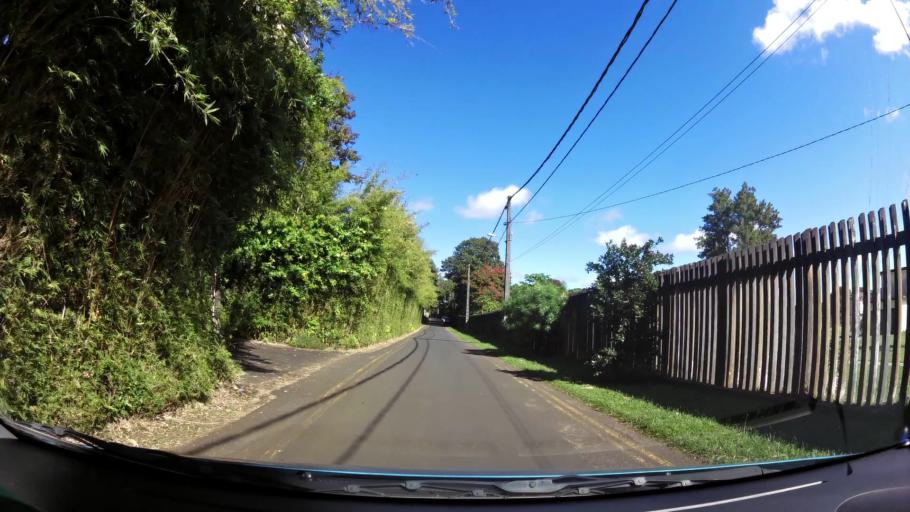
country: MU
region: Plaines Wilhems
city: Vacoas
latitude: -20.2974
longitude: 57.4983
